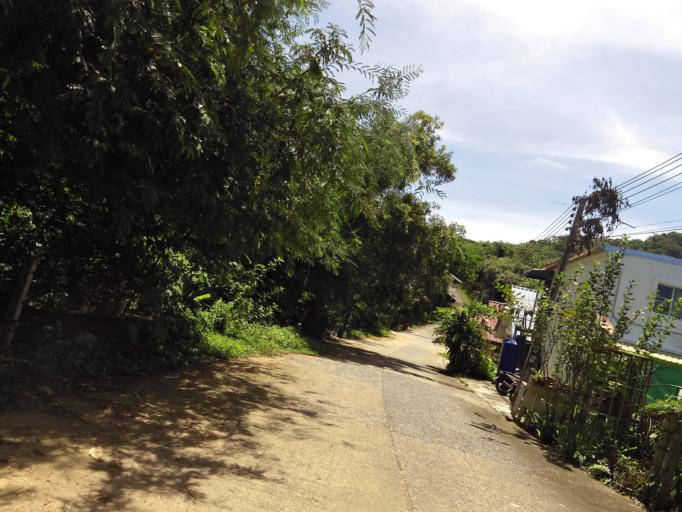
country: TH
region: Phuket
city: Ban Karon
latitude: 7.8472
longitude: 98.3042
